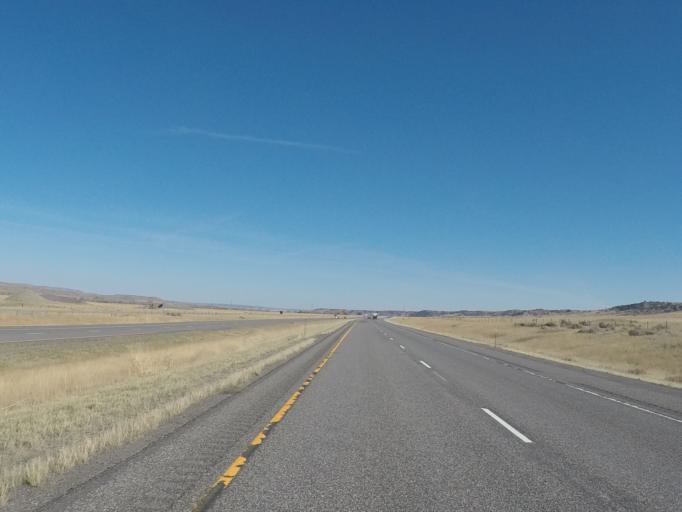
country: US
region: Montana
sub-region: Sweet Grass County
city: Big Timber
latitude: 45.7463
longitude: -110.1790
